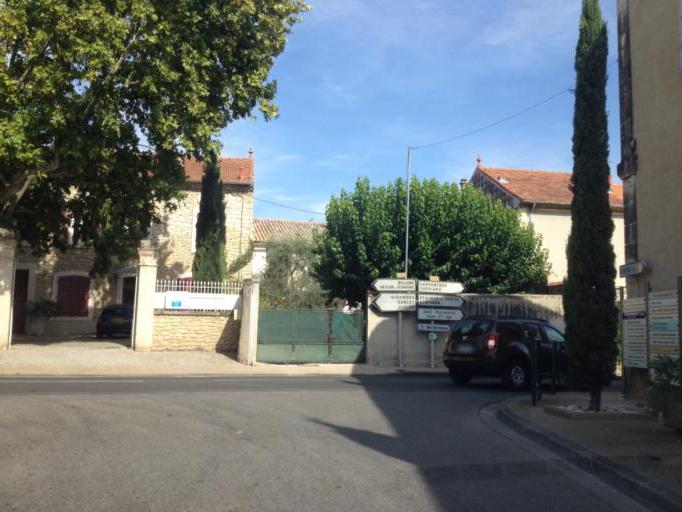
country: FR
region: Provence-Alpes-Cote d'Azur
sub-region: Departement du Vaucluse
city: Vacqueyras
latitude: 44.1378
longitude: 4.9850
